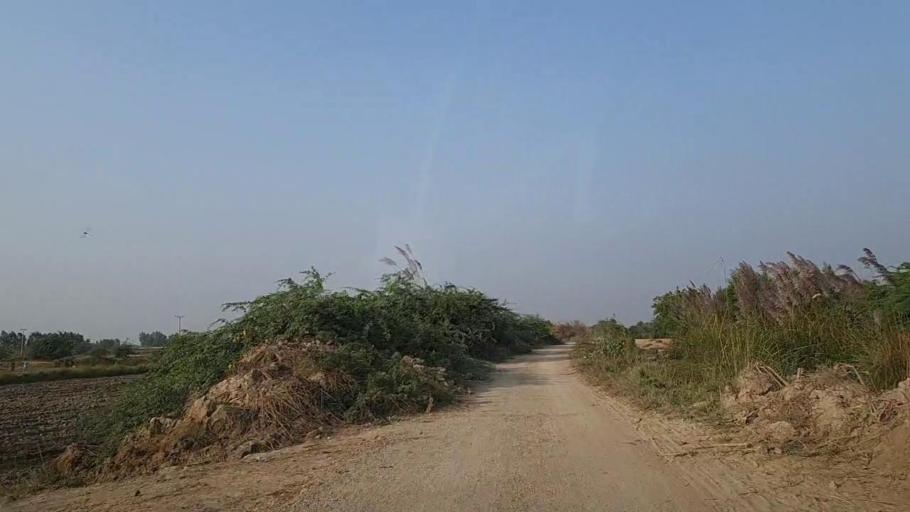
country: PK
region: Sindh
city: Thatta
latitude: 24.6734
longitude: 67.7832
